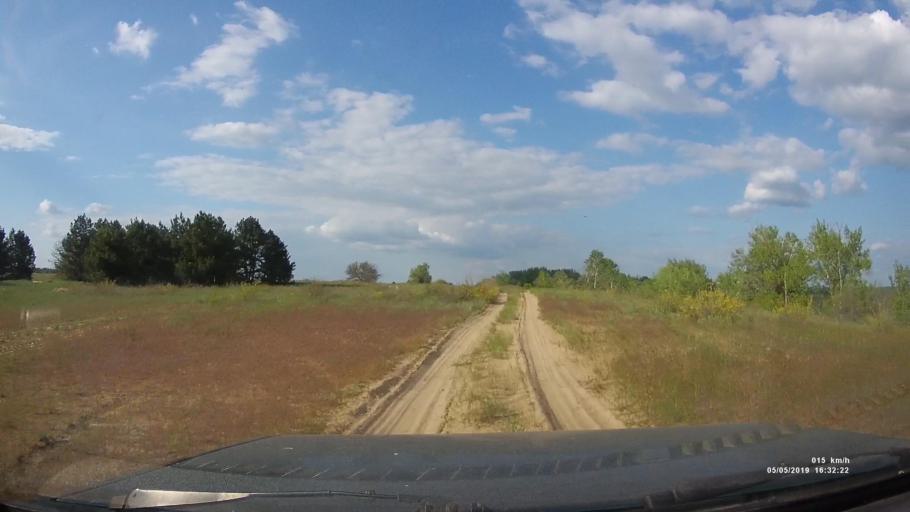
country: RU
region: Rostov
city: Ust'-Donetskiy
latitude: 47.7787
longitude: 41.0142
